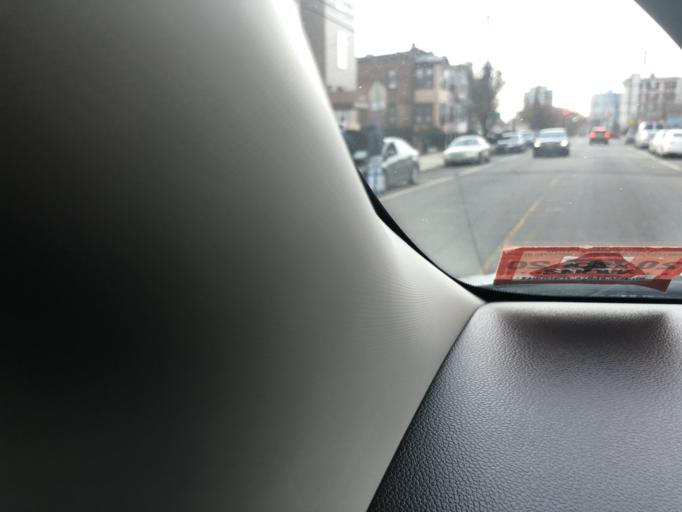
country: US
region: New Jersey
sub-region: Essex County
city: Newark
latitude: 40.7172
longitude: -74.1954
